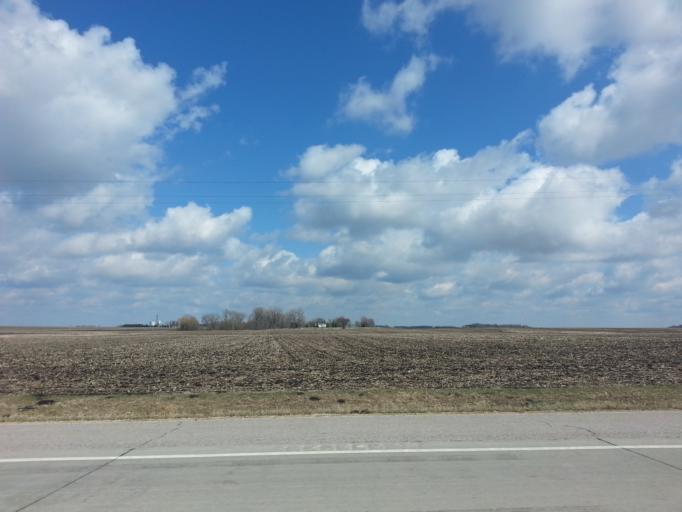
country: US
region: Minnesota
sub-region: Dodge County
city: Dodge Center
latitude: 44.1130
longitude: -92.8995
